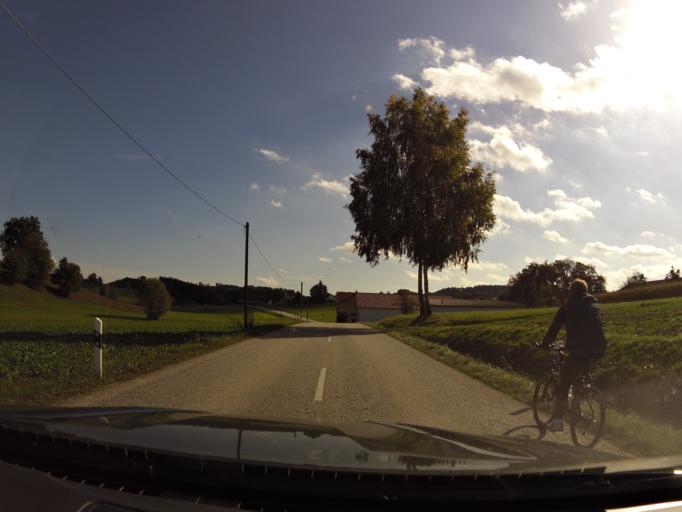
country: DE
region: Bavaria
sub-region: Lower Bavaria
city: Tiefenbach
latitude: 48.4843
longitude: 12.1105
